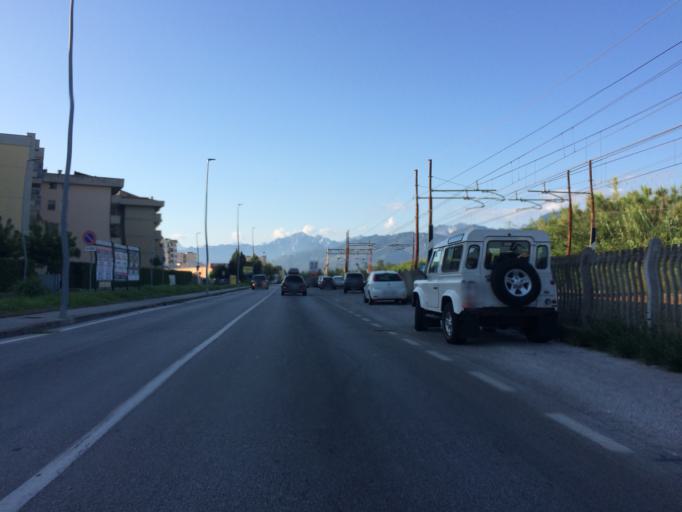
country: IT
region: Tuscany
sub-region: Provincia di Lucca
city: Viareggio
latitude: 43.8825
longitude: 10.2511
